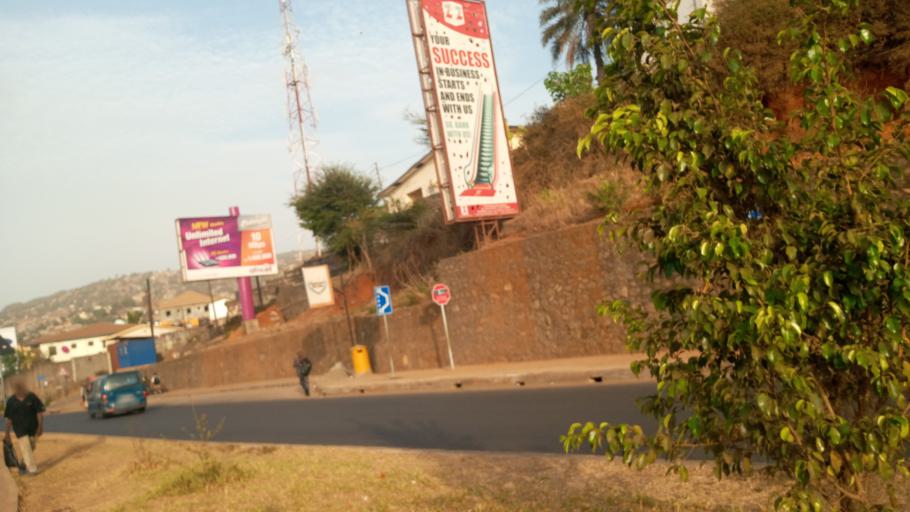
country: SL
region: Western Area
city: Freetown
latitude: 8.4693
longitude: -13.2451
